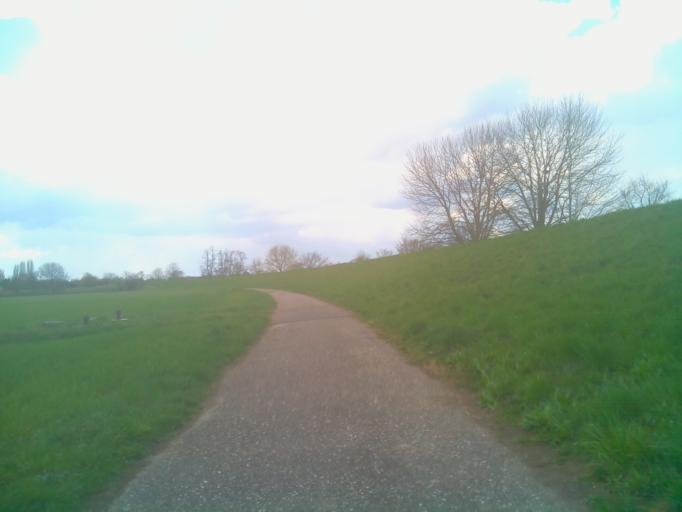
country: DE
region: Baden-Wuerttemberg
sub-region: Karlsruhe Region
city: Ilvesheim
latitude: 49.4743
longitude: 8.5777
